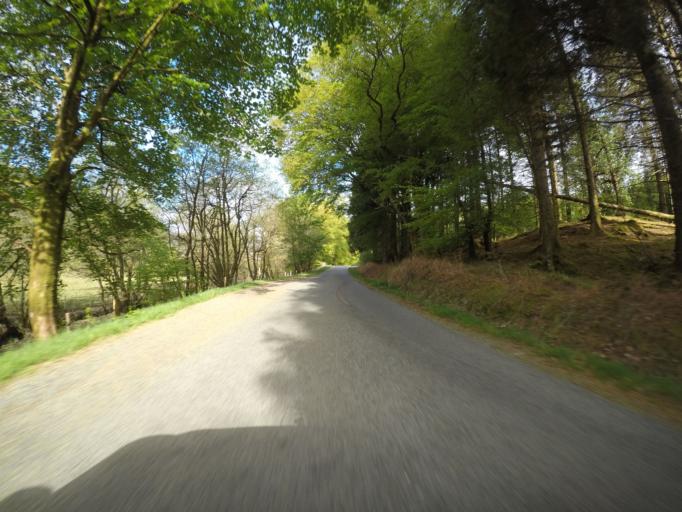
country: GB
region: Scotland
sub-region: Highland
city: Fort William
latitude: 56.6819
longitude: -5.0906
